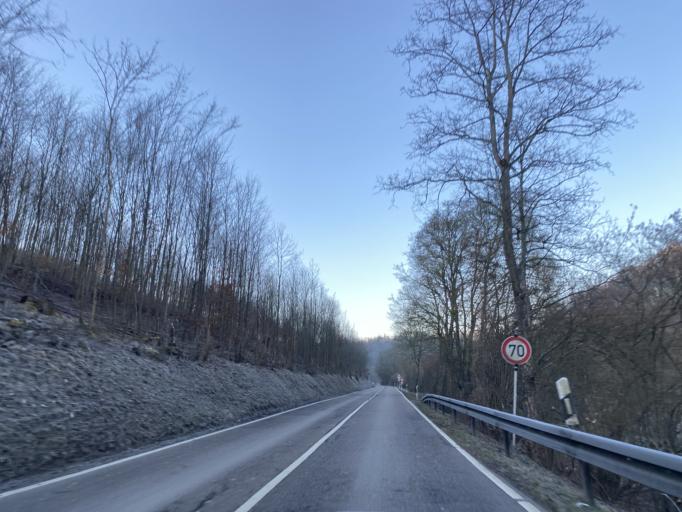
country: DE
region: Baden-Wuerttemberg
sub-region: Regierungsbezirk Stuttgart
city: Eberdingen
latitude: 48.8585
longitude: 8.9625
